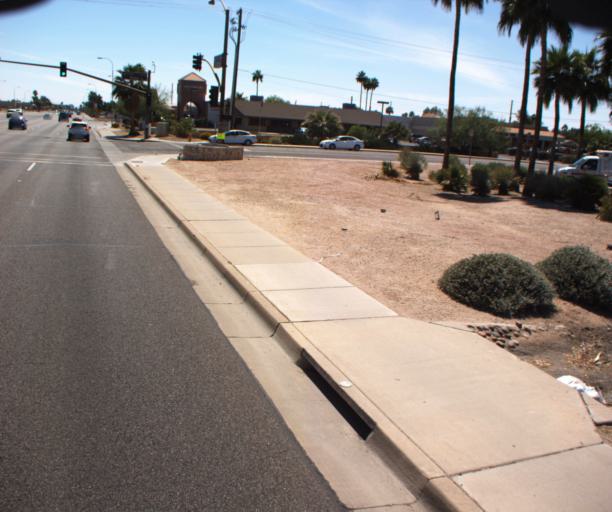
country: US
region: Arizona
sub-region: Maricopa County
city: San Carlos
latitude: 33.3284
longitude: -111.8418
